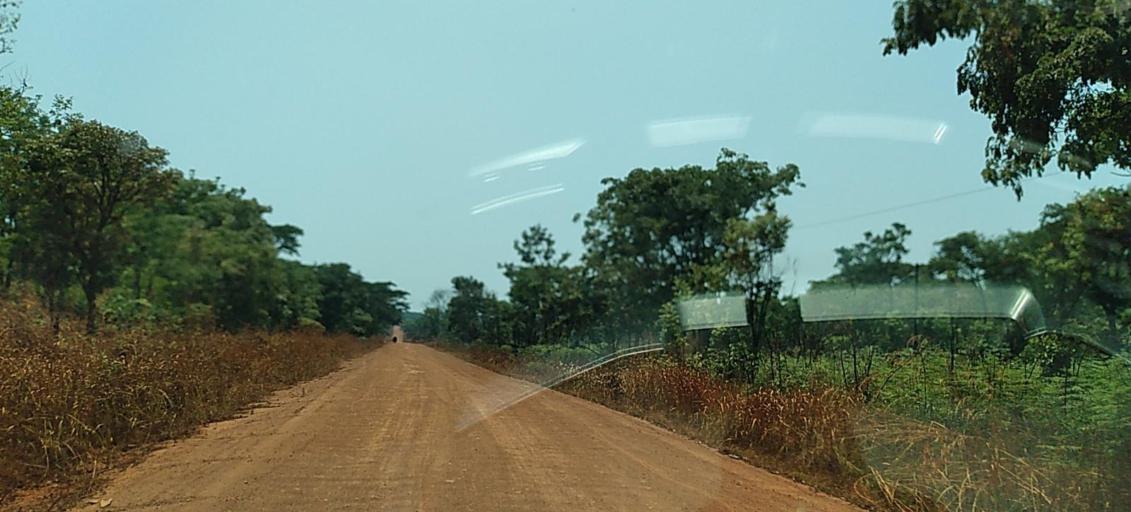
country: ZM
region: North-Western
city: Kansanshi
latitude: -11.9871
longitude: 26.8487
